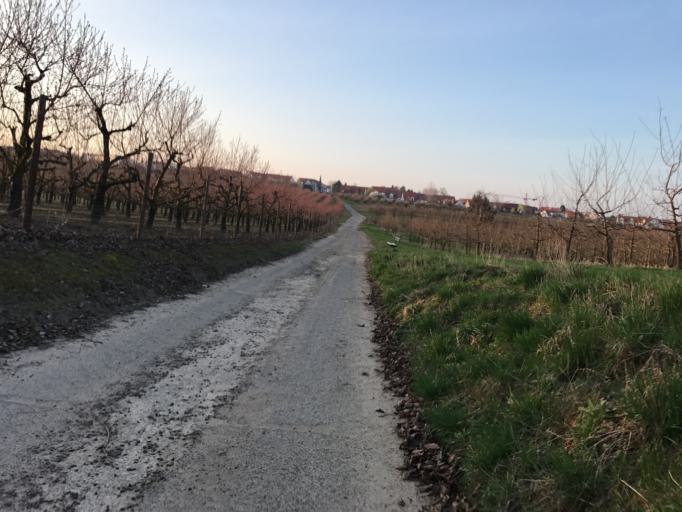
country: DE
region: Rheinland-Pfalz
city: Ober-Olm
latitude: 49.9684
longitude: 8.1940
